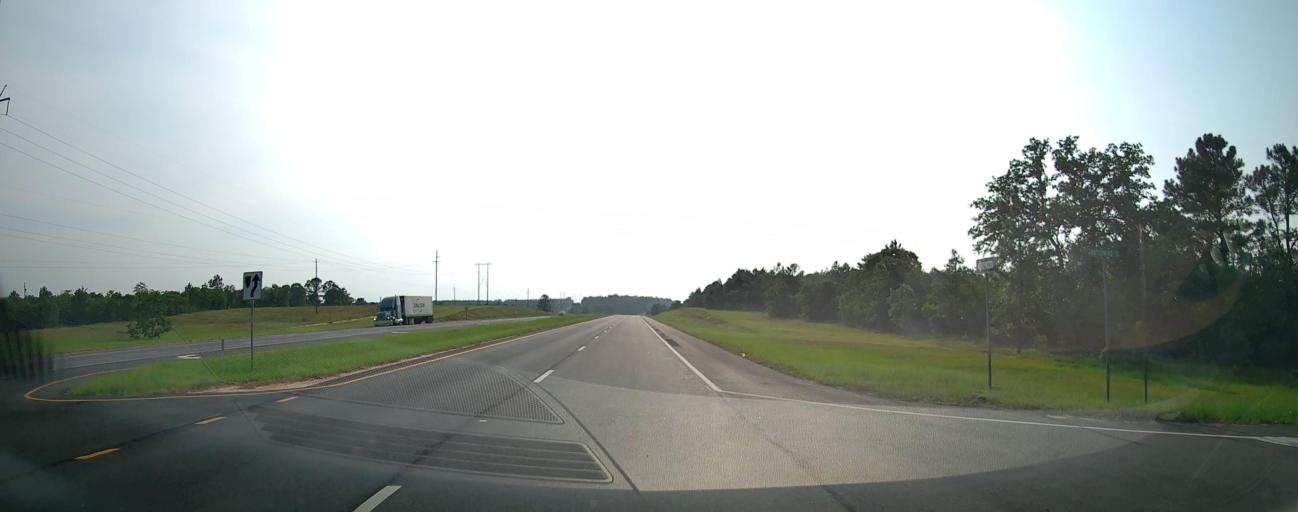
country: US
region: Georgia
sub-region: Taylor County
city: Butler
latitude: 32.5927
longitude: -84.3860
